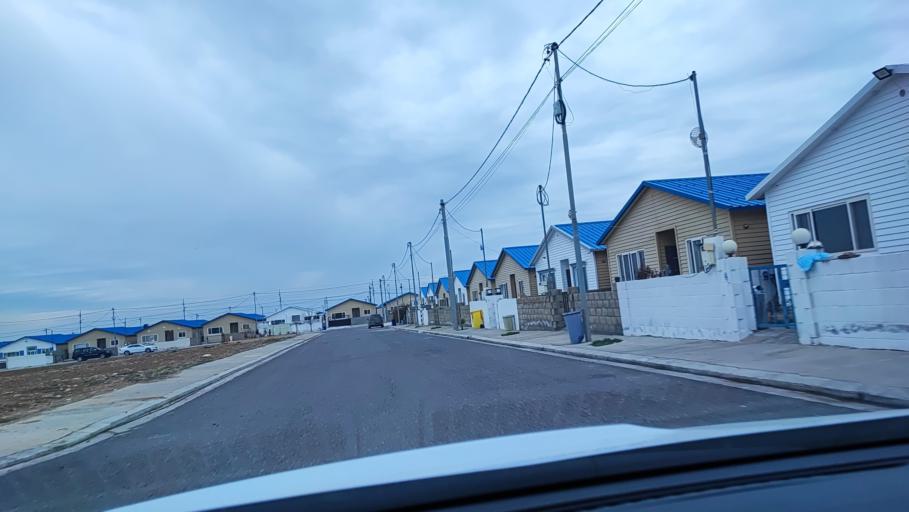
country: IQ
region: Arbil
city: Erbil
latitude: 36.2865
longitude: 44.0804
